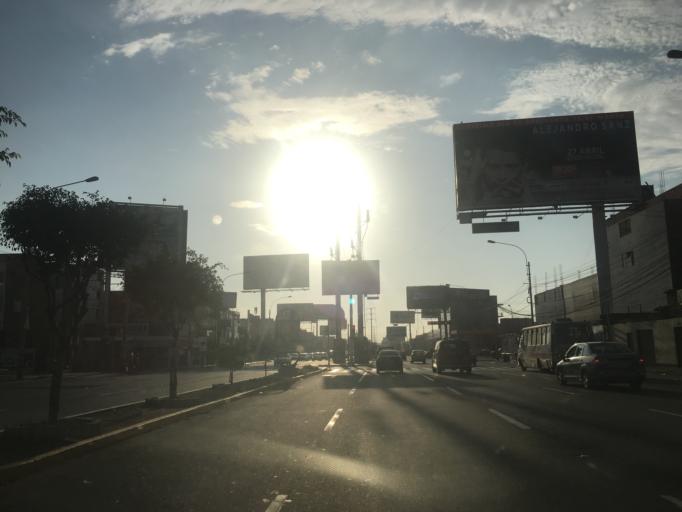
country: PE
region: Lima
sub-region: Lima
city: San Isidro
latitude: -12.0821
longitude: -77.0698
